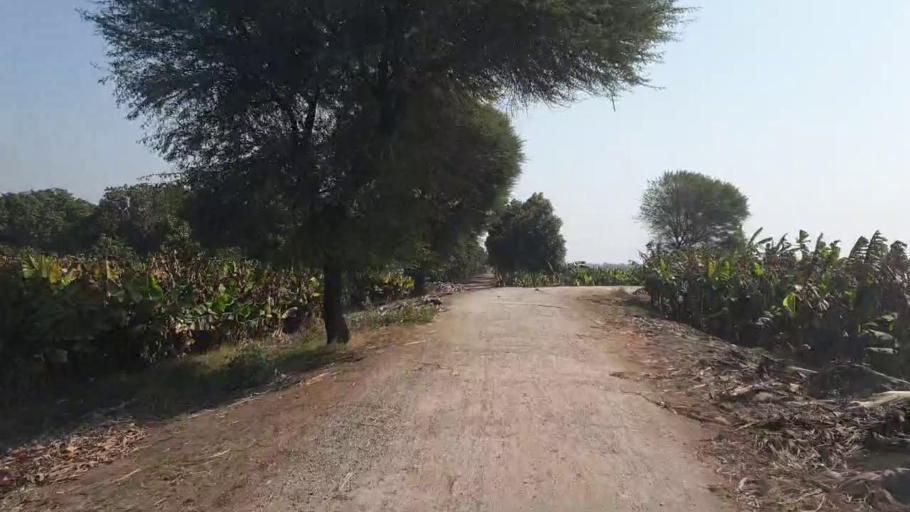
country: PK
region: Sindh
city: Tando Jam
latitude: 25.3423
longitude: 68.6013
